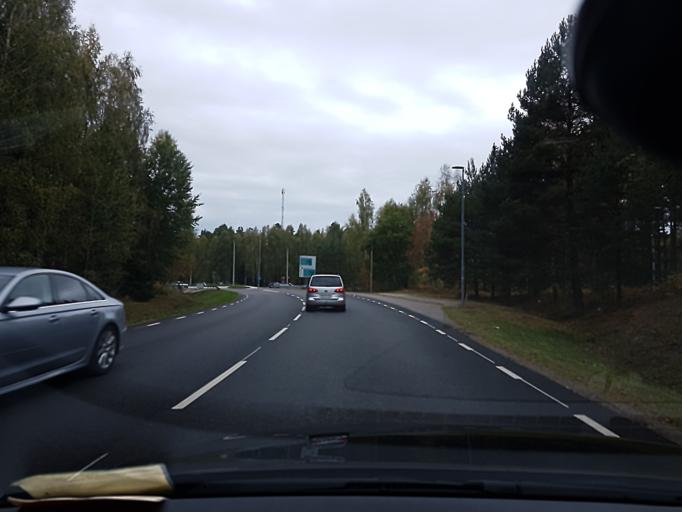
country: SE
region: Kronoberg
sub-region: Vaxjo Kommun
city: Vaexjoe
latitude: 56.9048
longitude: 14.7965
